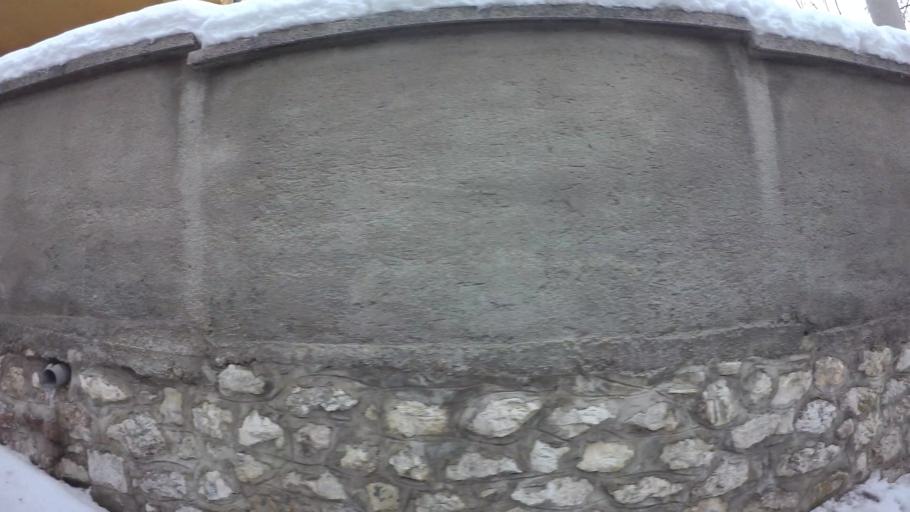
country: BA
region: Federation of Bosnia and Herzegovina
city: Kobilja Glava
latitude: 43.8703
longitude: 18.4385
